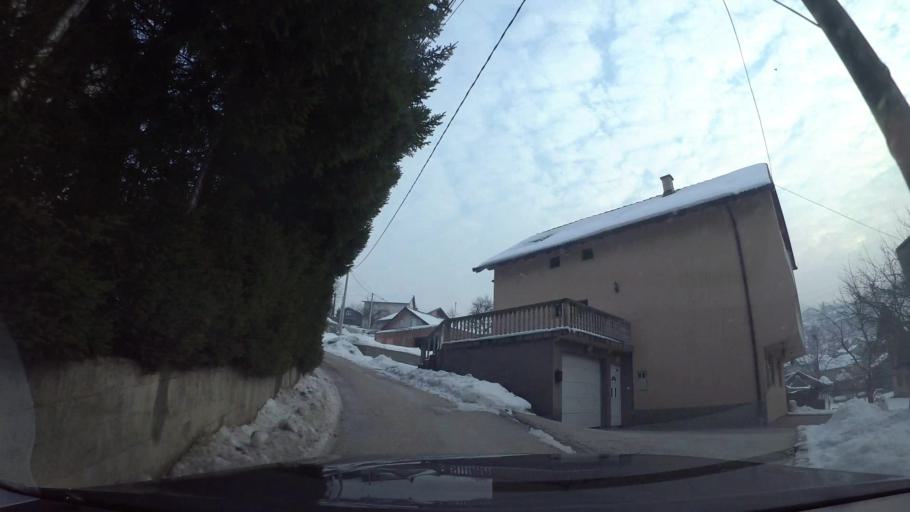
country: BA
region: Federation of Bosnia and Herzegovina
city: Hotonj
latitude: 43.8925
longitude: 18.3709
